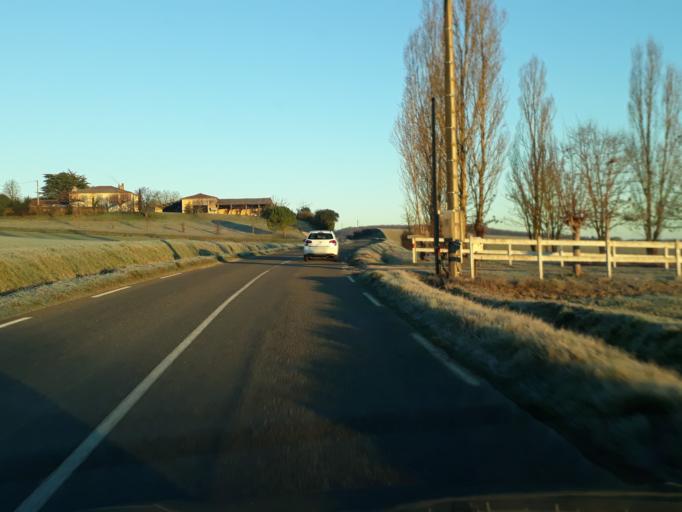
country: FR
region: Midi-Pyrenees
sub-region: Departement du Gers
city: Pavie
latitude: 43.6232
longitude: 0.6392
